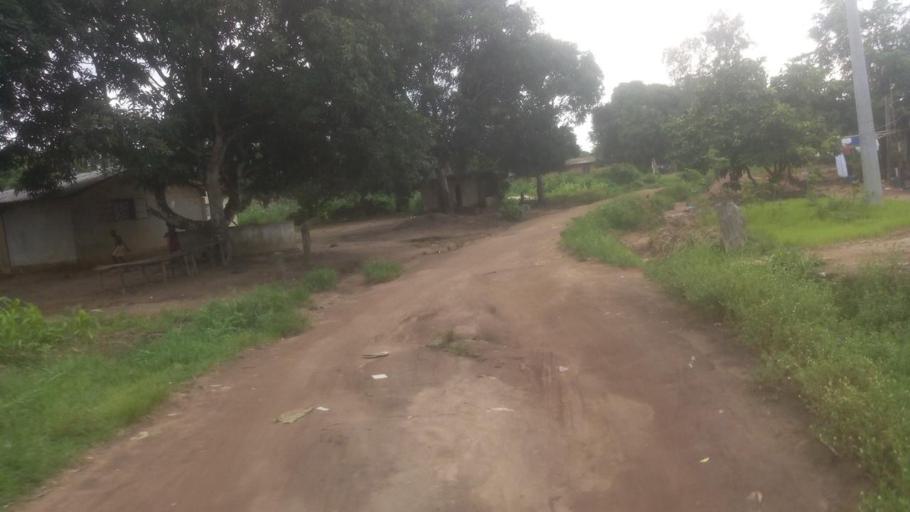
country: SL
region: Northern Province
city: Masoyila
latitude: 8.6075
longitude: -13.1940
